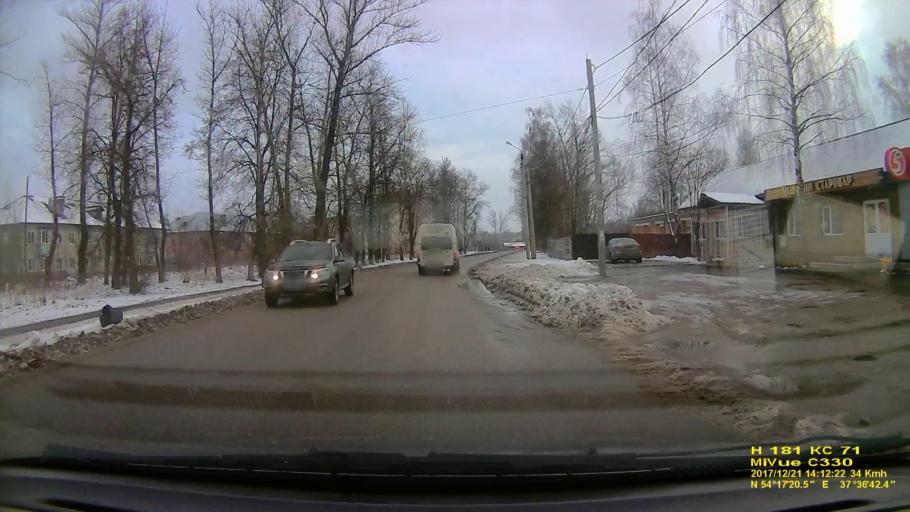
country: RU
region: Tula
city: Gorelki
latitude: 54.2889
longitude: 37.6120
